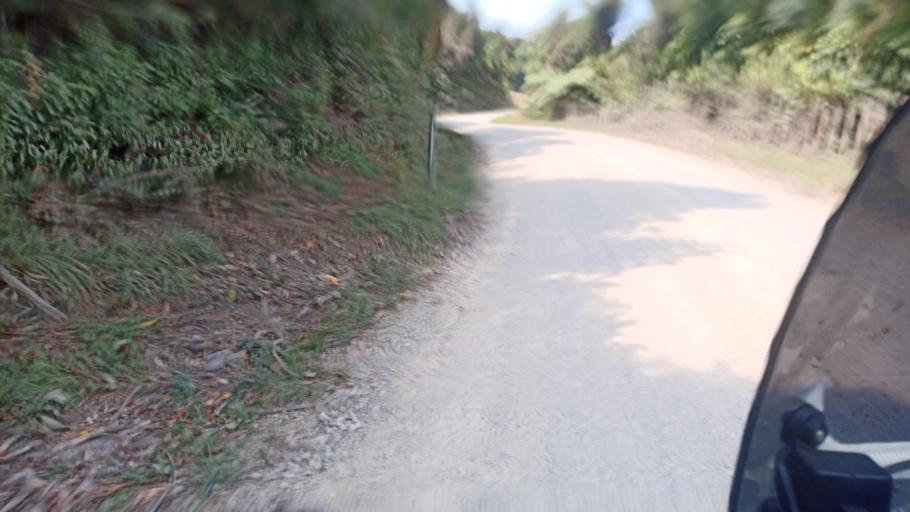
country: NZ
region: Bay of Plenty
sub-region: Opotiki District
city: Opotiki
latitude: -37.6509
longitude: 178.1387
